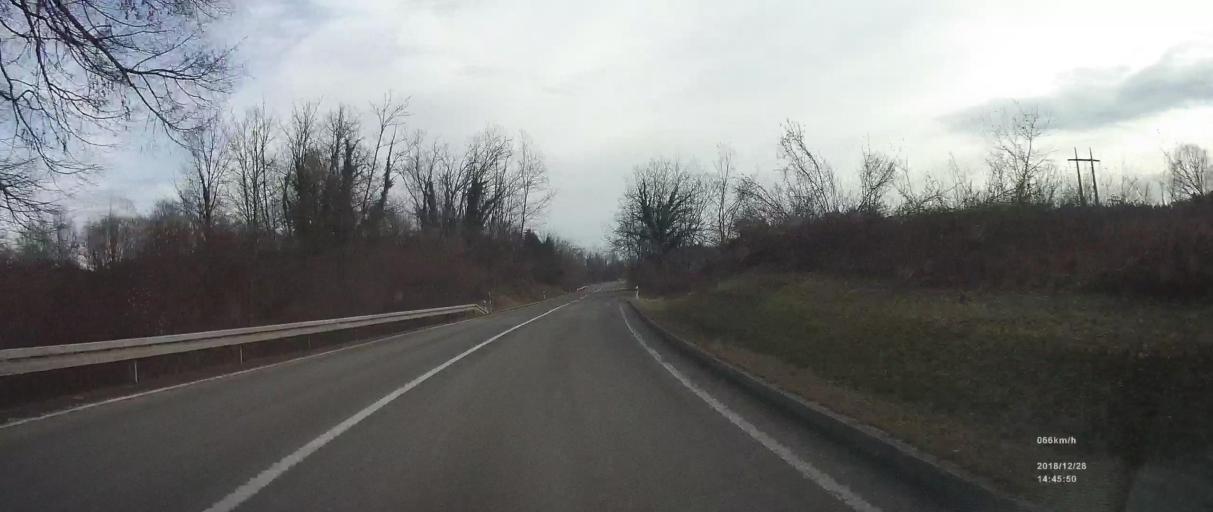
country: SI
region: Crnomelj
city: Crnomelj
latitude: 45.4507
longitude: 15.3089
